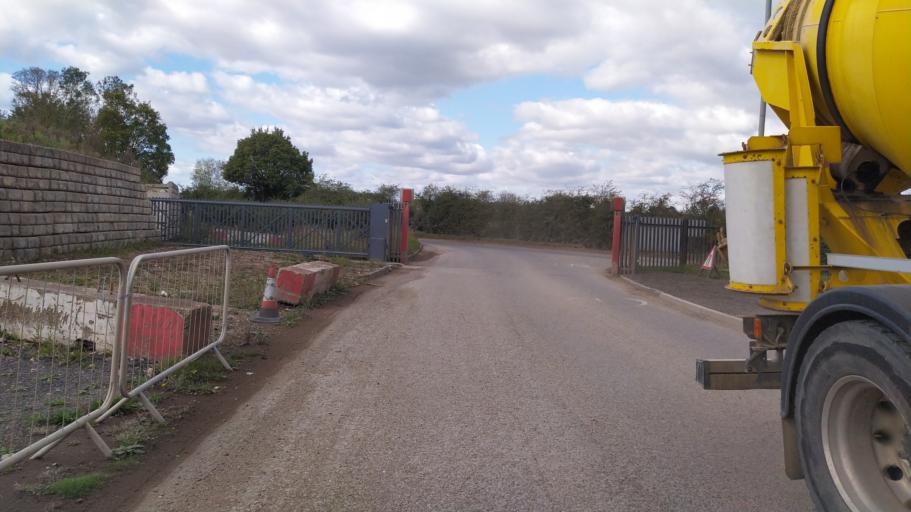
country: GB
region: England
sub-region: West Berkshire
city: Calcot
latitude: 51.4250
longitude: -1.0219
